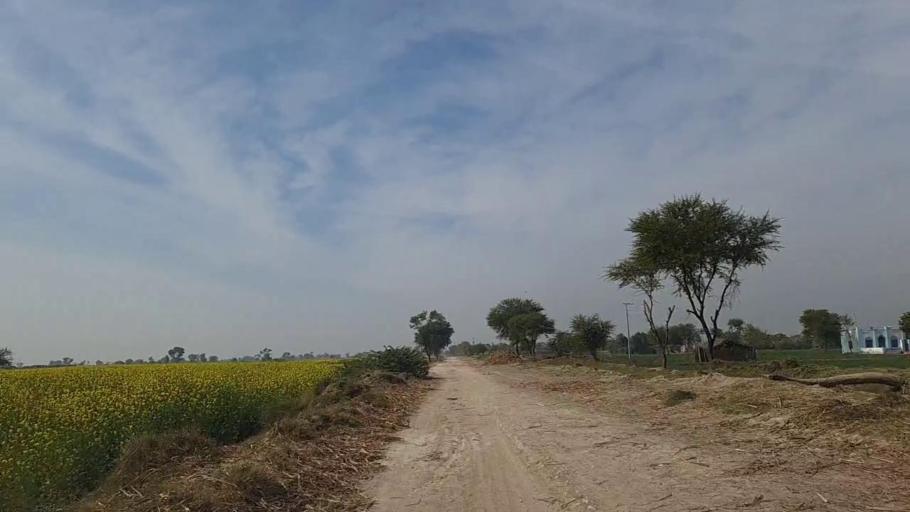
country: PK
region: Sindh
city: Nawabshah
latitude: 26.3276
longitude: 68.4294
